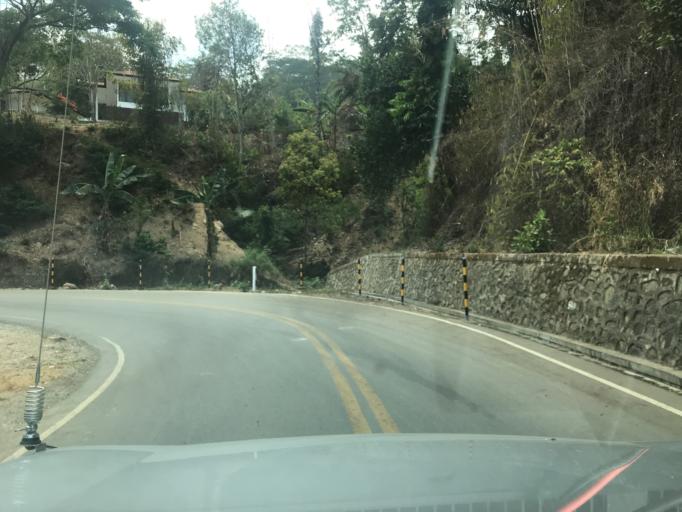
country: TL
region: Dili
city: Dili
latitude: -8.5991
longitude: 125.5859
